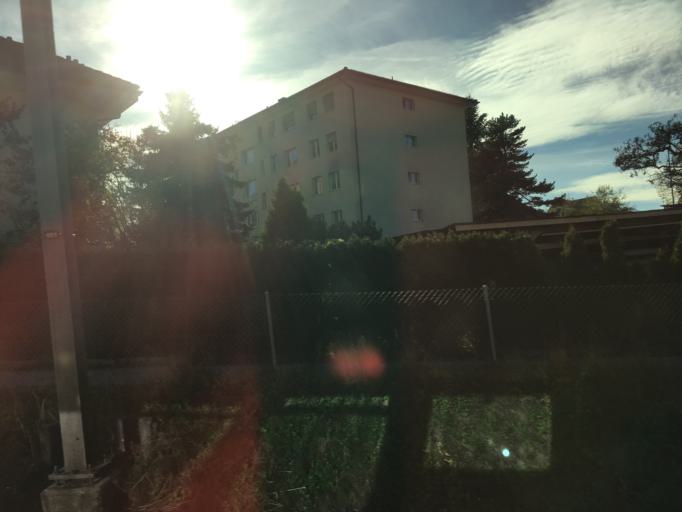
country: CH
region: Zurich
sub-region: Bezirk Horgen
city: Richterswil / Burghalde
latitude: 47.1931
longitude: 8.6825
